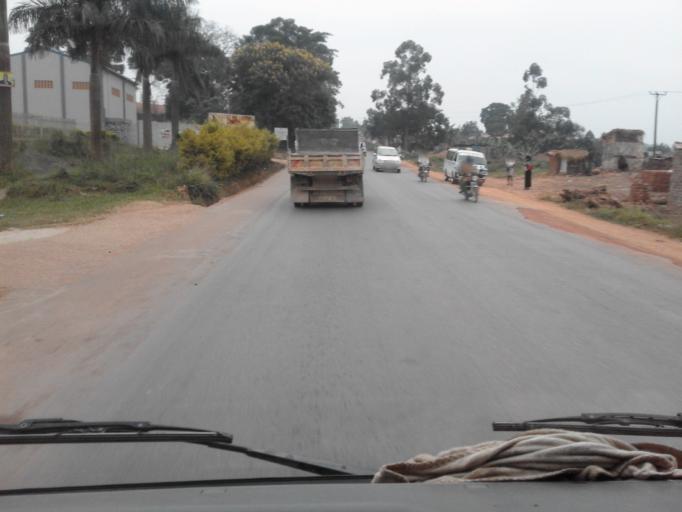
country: UG
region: Central Region
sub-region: Wakiso District
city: Bweyogerere
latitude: 0.3669
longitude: 32.7062
